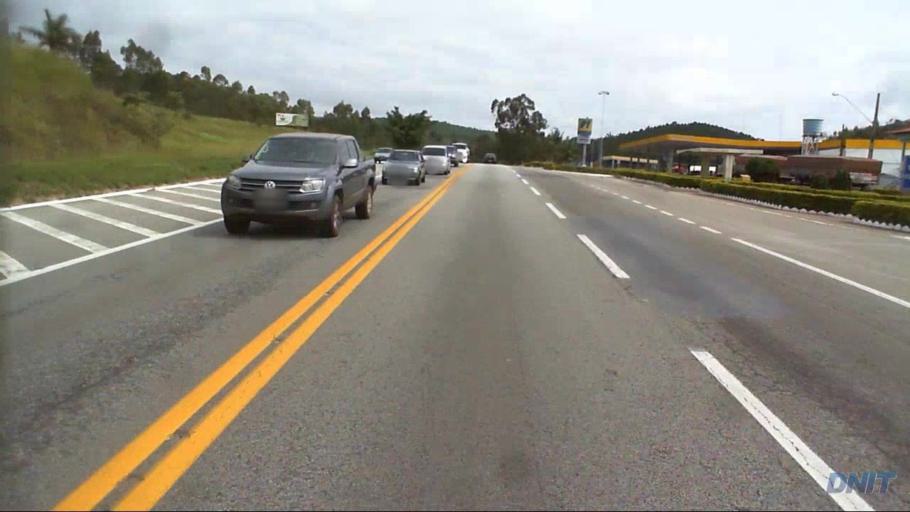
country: BR
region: Minas Gerais
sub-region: Caete
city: Caete
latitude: -19.7242
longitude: -43.5838
